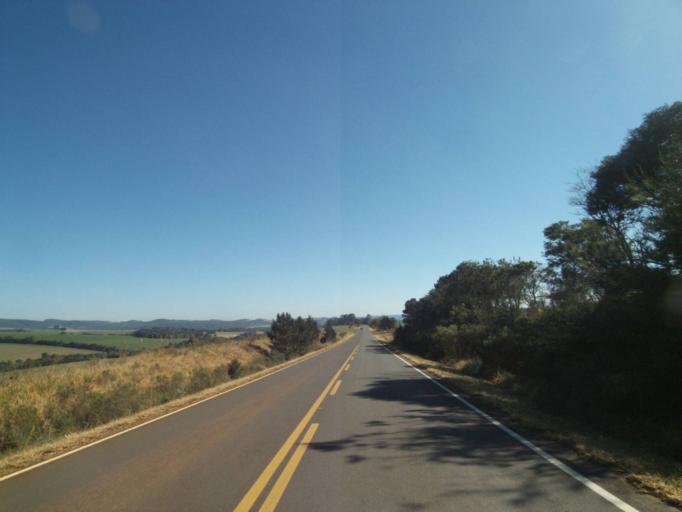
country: BR
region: Parana
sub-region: Tibagi
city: Tibagi
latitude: -24.4911
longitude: -50.4670
